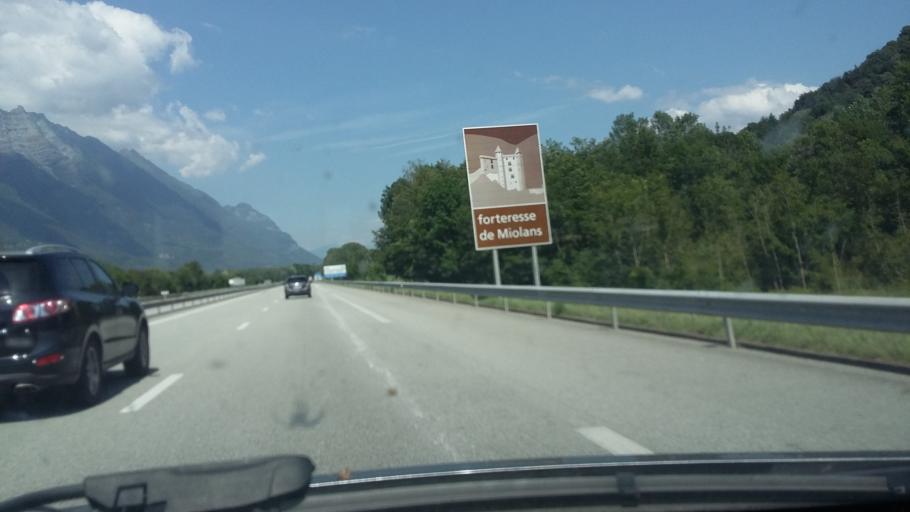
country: FR
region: Rhone-Alpes
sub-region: Departement de la Savoie
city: Coise-Saint-Jean-Pied-Gauthier
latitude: 45.5399
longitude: 6.1377
